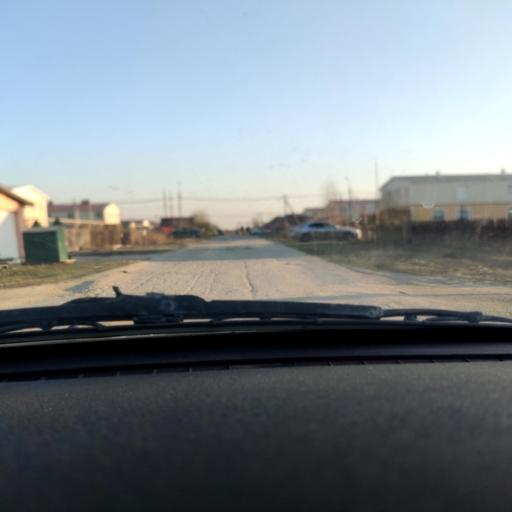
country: RU
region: Samara
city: Podstepki
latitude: 53.5714
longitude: 49.1191
